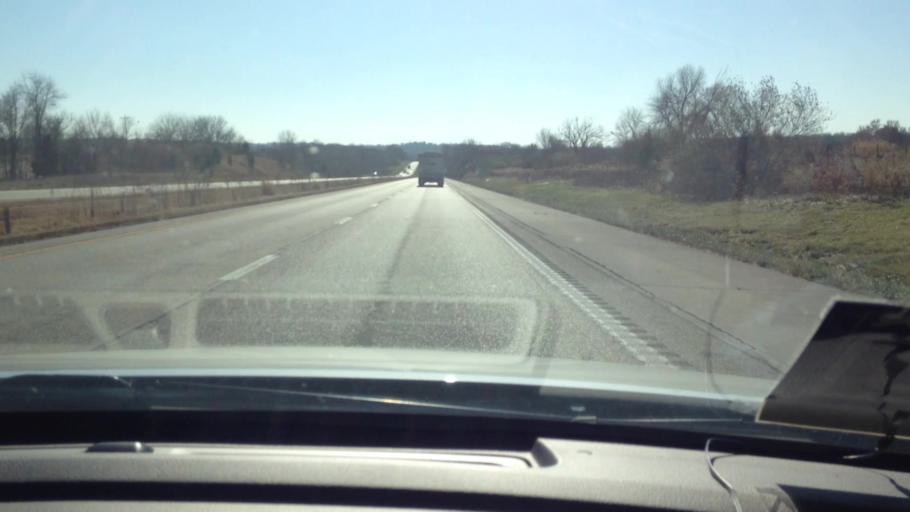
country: US
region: Missouri
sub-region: Platte County
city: Platte City
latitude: 39.4009
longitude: -94.7898
